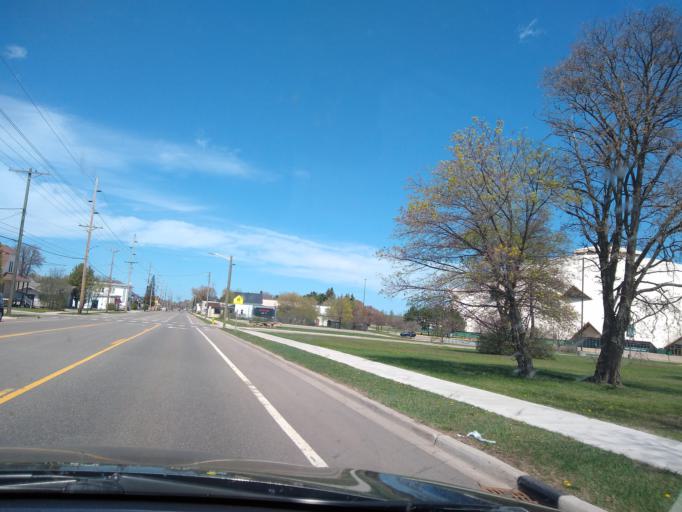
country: US
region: Michigan
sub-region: Marquette County
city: Marquette
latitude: 46.5585
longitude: -87.3962
